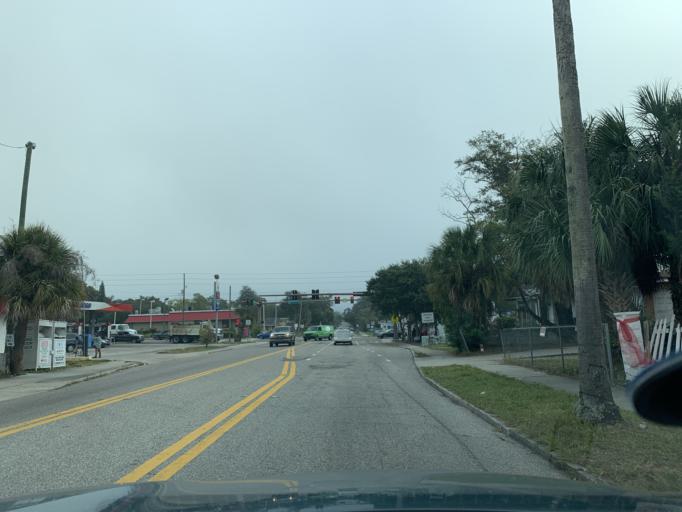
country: US
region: Florida
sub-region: Pinellas County
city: Saint Petersburg
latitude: 27.7521
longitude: -82.6475
